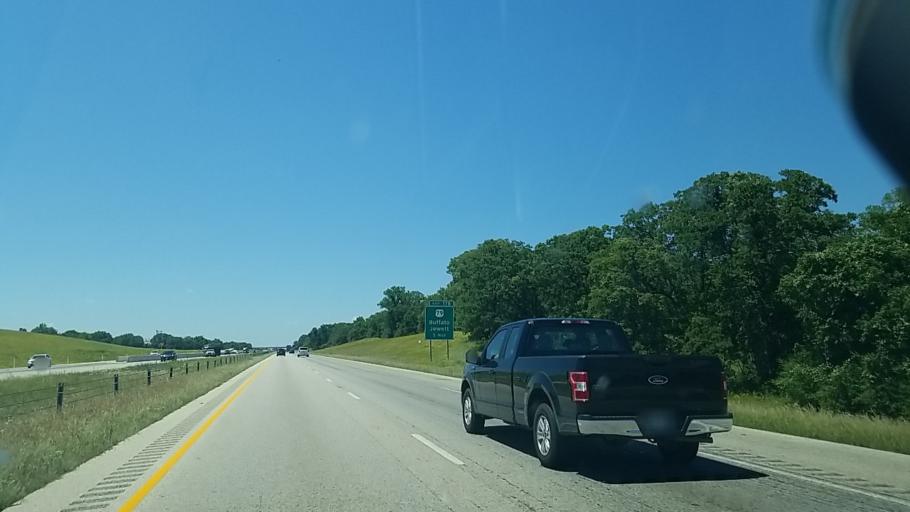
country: US
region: Texas
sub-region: Leon County
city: Buffalo
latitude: 31.4347
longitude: -96.0612
